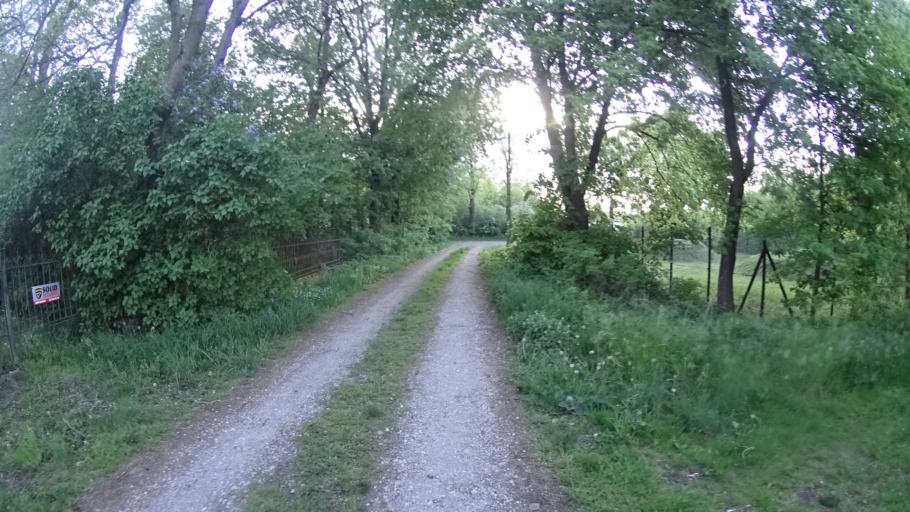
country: PL
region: Masovian Voivodeship
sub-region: Powiat warszawski zachodni
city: Jozefow
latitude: 52.1998
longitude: 20.7412
